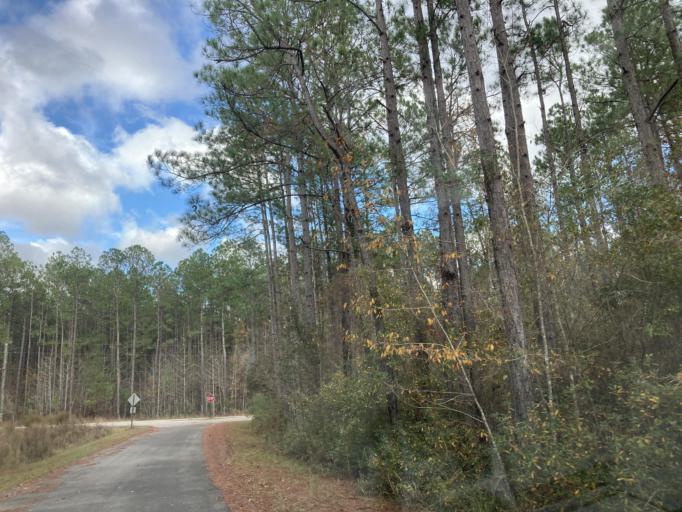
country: US
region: Mississippi
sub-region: Lamar County
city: Purvis
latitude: 31.1755
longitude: -89.5788
